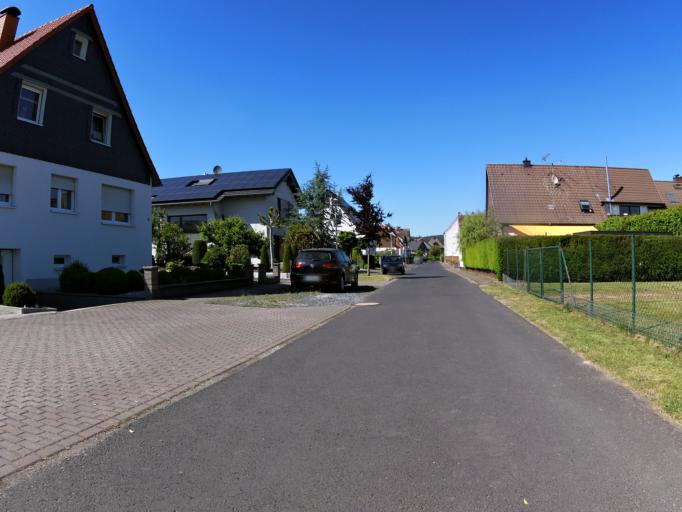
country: DE
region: Thuringia
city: Dippach
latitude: 50.9460
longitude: 10.0416
